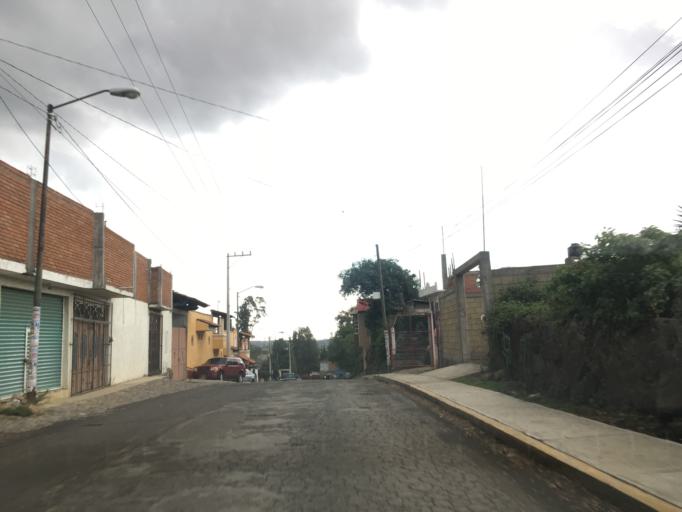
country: MX
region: Michoacan
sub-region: Morelia
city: La Mintzita (Piedra Dura)
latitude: 19.5975
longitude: -101.2910
